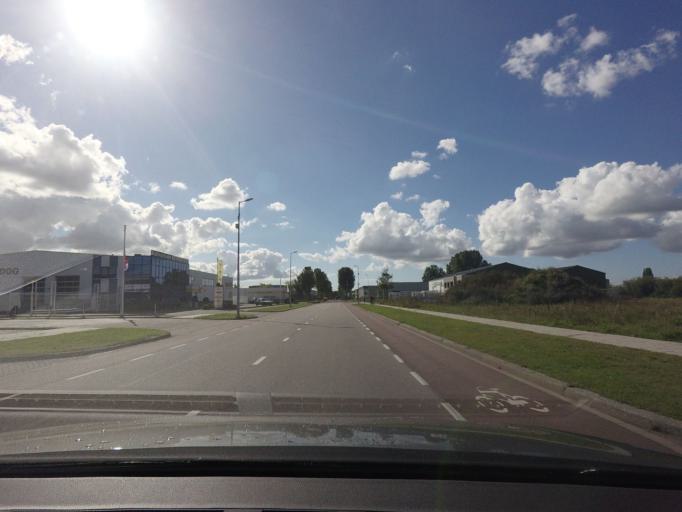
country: NL
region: North Holland
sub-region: Gemeente Langedijk
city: Broek op Langedijk
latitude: 52.6563
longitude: 4.7960
